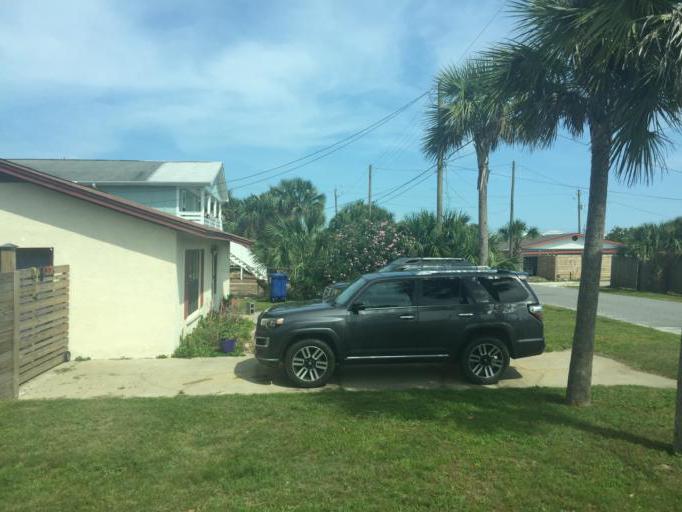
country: US
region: Florida
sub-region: Bay County
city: Laguna Beach
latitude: 30.2467
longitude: -85.9357
